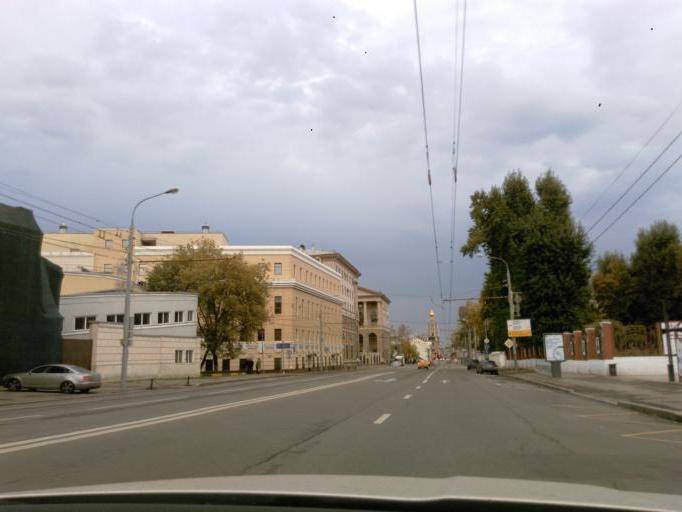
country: RU
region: Moscow
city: Moscow
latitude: 55.7711
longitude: 37.6107
